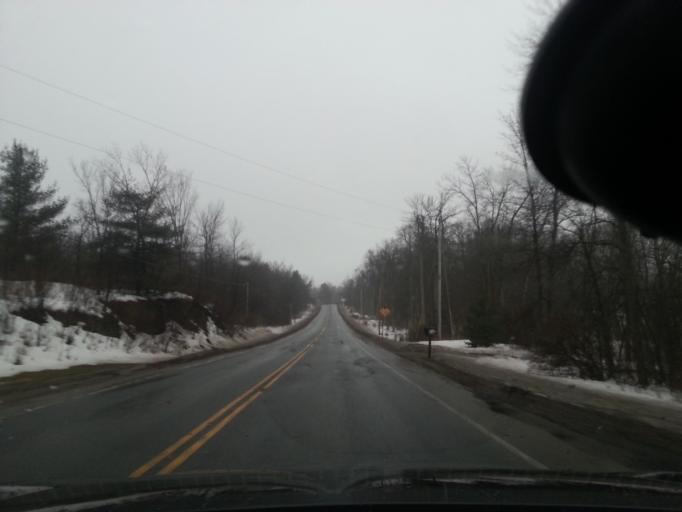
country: US
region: New York
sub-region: St. Lawrence County
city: Canton
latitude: 44.5048
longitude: -75.3409
